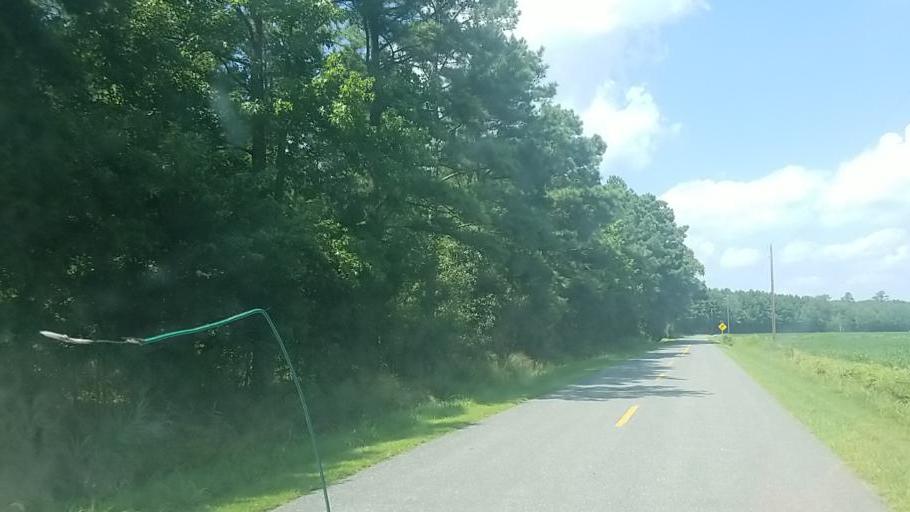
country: US
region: Maryland
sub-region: Dorchester County
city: Hurlock
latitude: 38.4678
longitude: -75.8453
